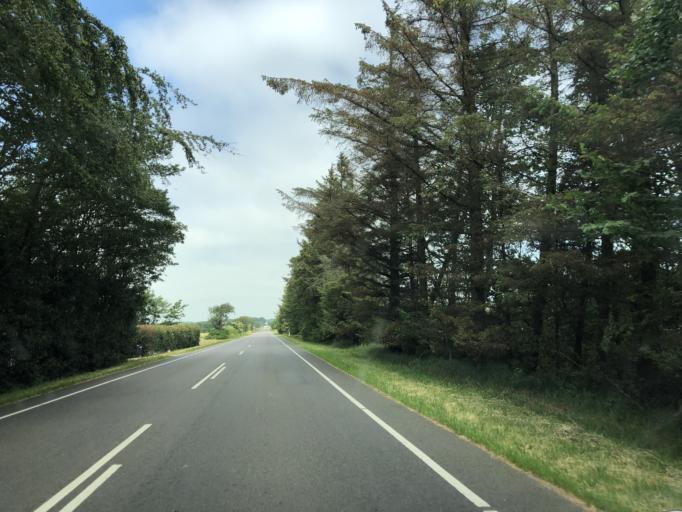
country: DK
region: South Denmark
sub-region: Varde Kommune
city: Varde
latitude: 55.6635
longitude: 8.4902
